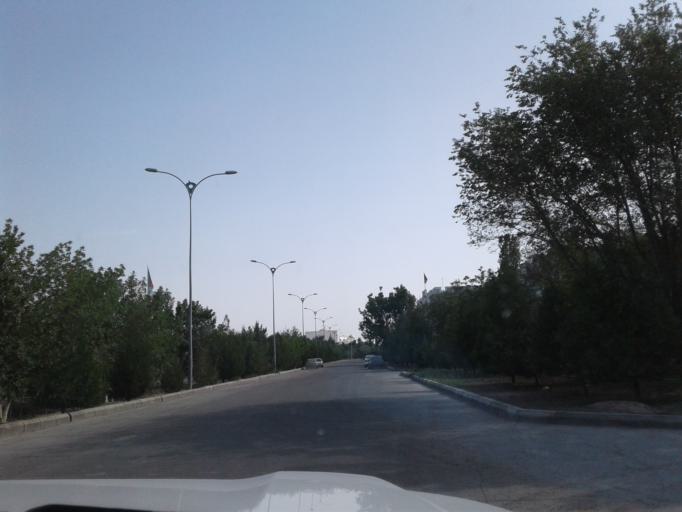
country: TM
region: Dasoguz
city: Dasoguz
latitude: 41.8332
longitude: 59.9645
